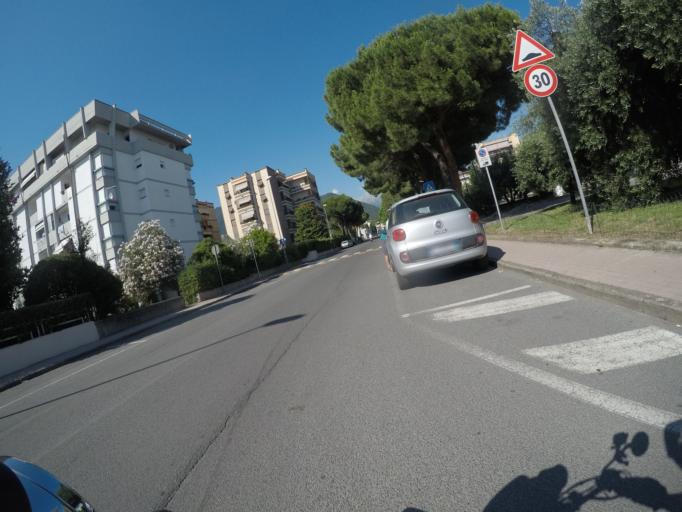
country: IT
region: Tuscany
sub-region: Provincia di Massa-Carrara
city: Massa
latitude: 44.0332
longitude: 10.1329
